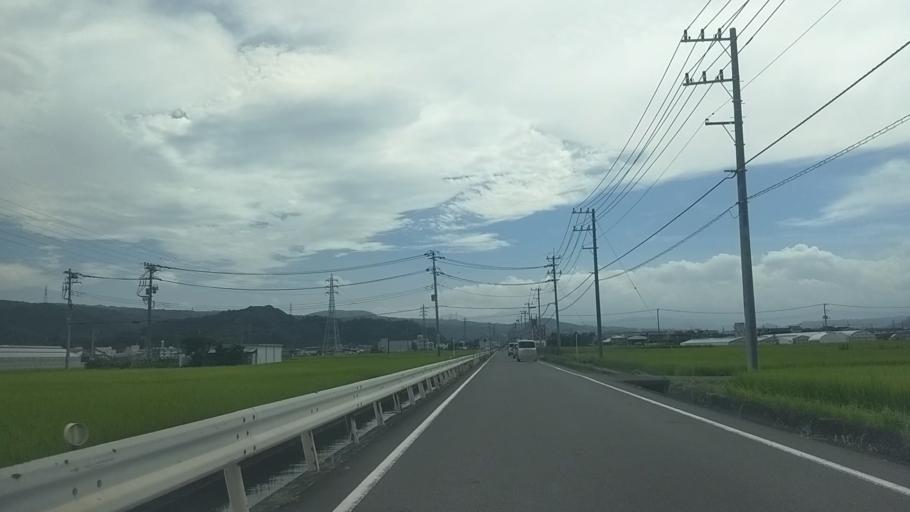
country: JP
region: Shizuoka
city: Mishima
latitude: 35.0630
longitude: 138.9470
